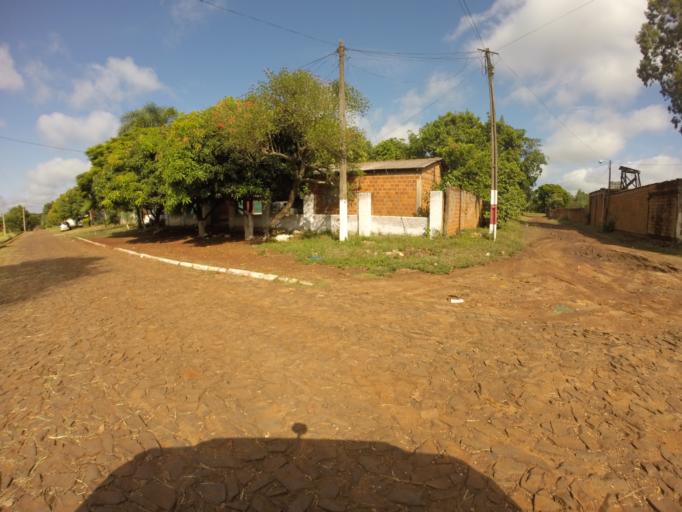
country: PY
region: Alto Parana
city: Ciudad del Este
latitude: -25.3980
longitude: -54.6499
